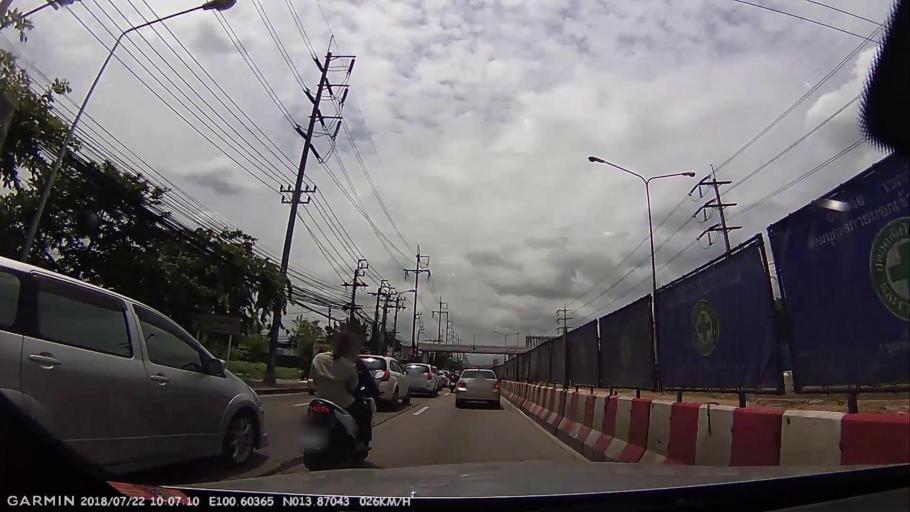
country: TH
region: Bangkok
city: Bang Khen
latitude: 13.8704
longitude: 100.6037
